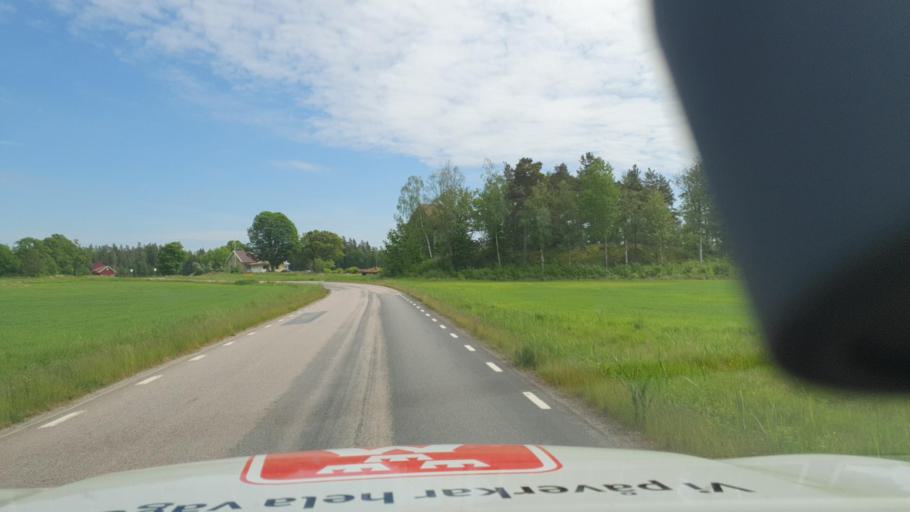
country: SE
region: Vaestra Goetaland
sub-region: Alingsas Kommun
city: Sollebrunn
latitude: 58.2135
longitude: 12.5292
